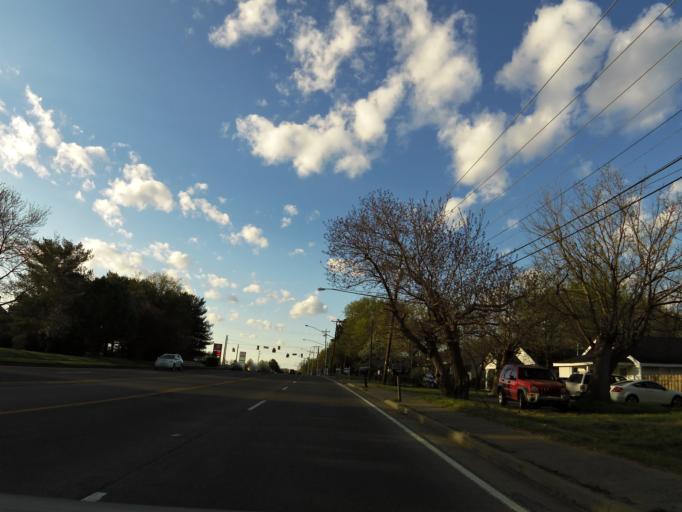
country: US
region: Tennessee
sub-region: Davidson County
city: Lakewood
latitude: 36.2153
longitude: -86.6230
